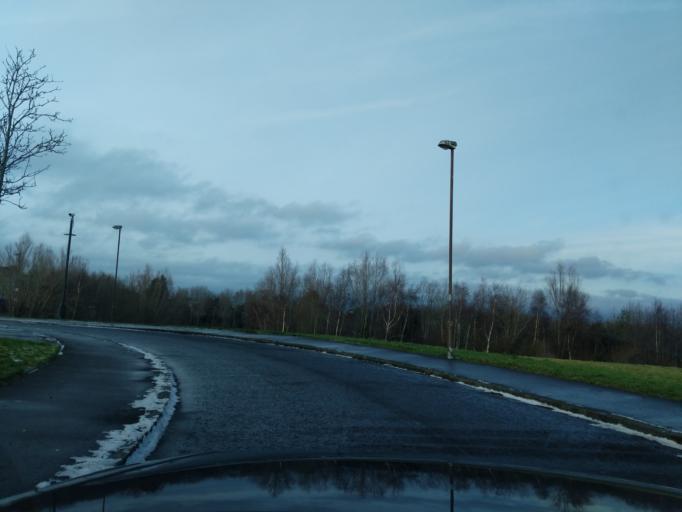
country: GB
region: Scotland
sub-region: Midlothian
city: Loanhead
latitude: 55.9001
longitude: -3.1514
